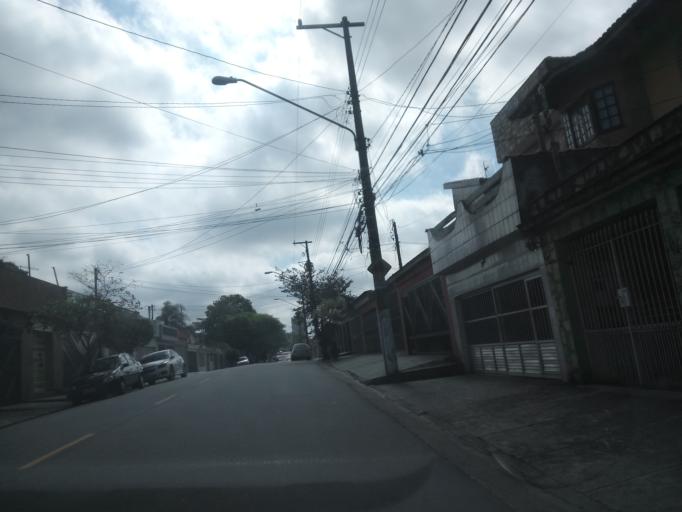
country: BR
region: Sao Paulo
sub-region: Sao Bernardo Do Campo
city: Sao Bernardo do Campo
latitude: -23.7243
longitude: -46.5659
